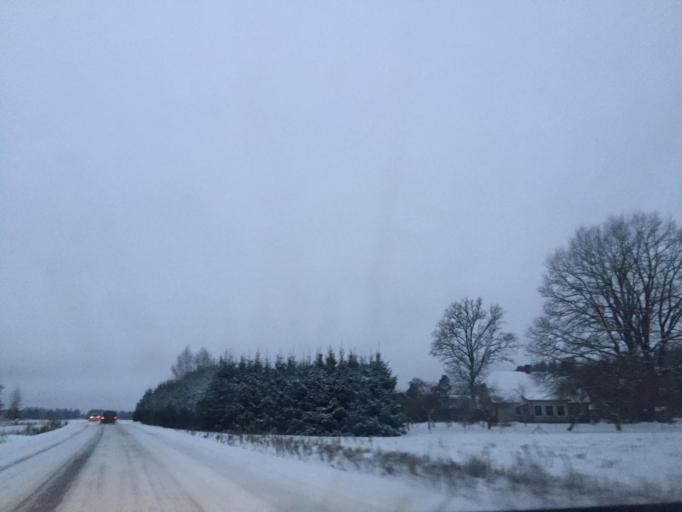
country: LV
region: Raunas
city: Rauna
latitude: 57.4288
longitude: 25.6011
